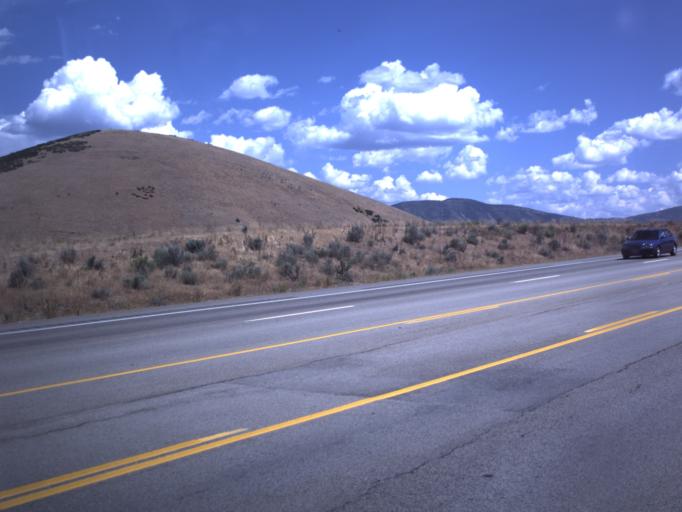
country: US
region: Utah
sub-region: Wasatch County
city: Midway
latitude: 40.4109
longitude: -111.5087
